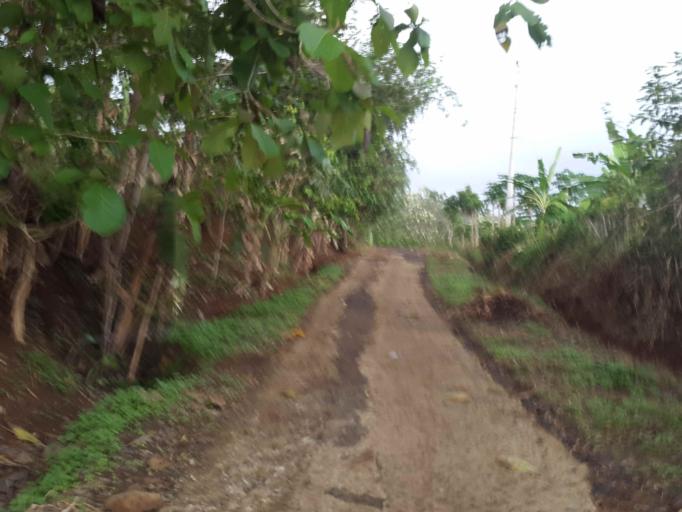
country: ID
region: Central Java
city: Limbangan
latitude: -7.2877
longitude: 108.7008
